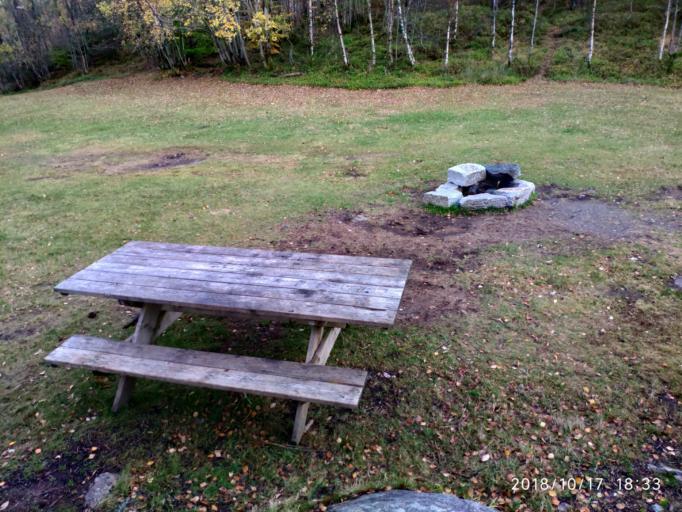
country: NO
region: Hordaland
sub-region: Askoy
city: Kleppesto
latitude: 60.3959
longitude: 5.2398
